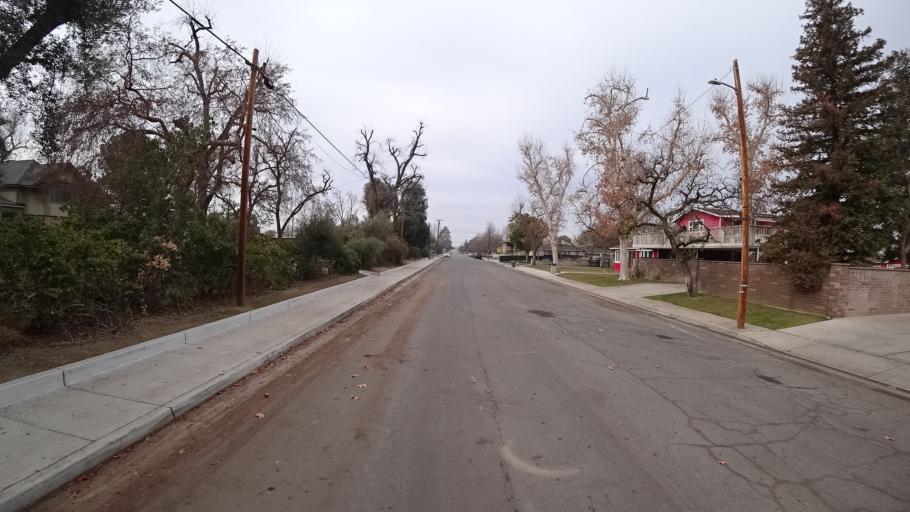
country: US
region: California
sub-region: Kern County
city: Bakersfield
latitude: 35.3632
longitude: -119.0299
